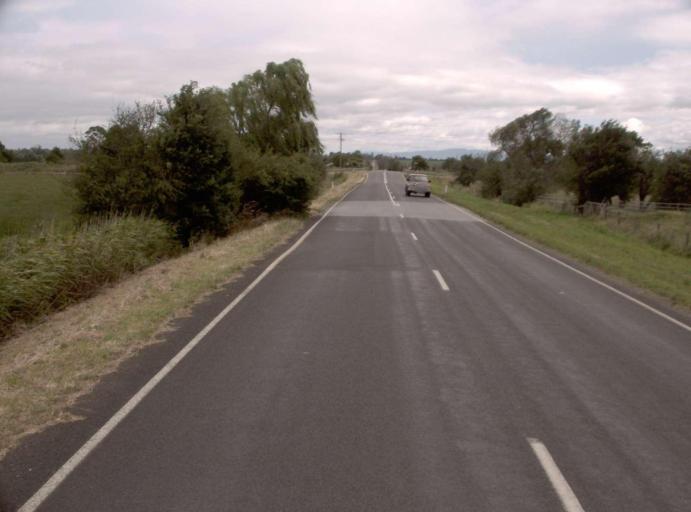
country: AU
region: Victoria
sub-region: Latrobe
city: Moe
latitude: -38.1874
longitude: 146.1485
